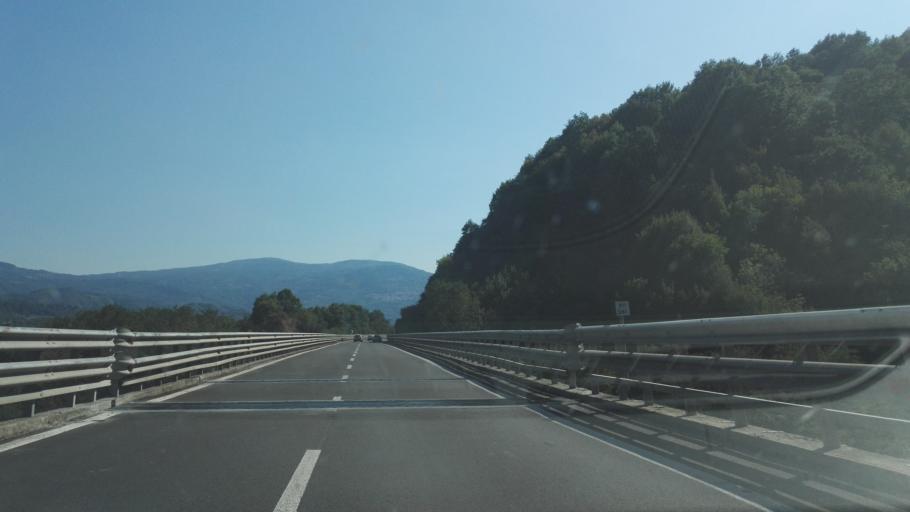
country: IT
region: Calabria
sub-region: Provincia di Cosenza
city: Altilia
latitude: 39.1365
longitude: 16.2729
